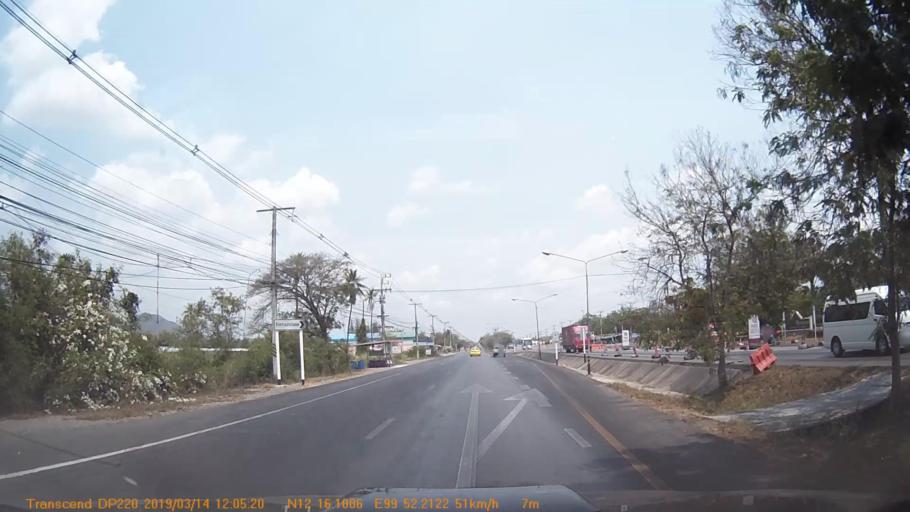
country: TH
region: Prachuap Khiri Khan
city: Sam Roi Yot
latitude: 12.2688
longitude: 99.8702
